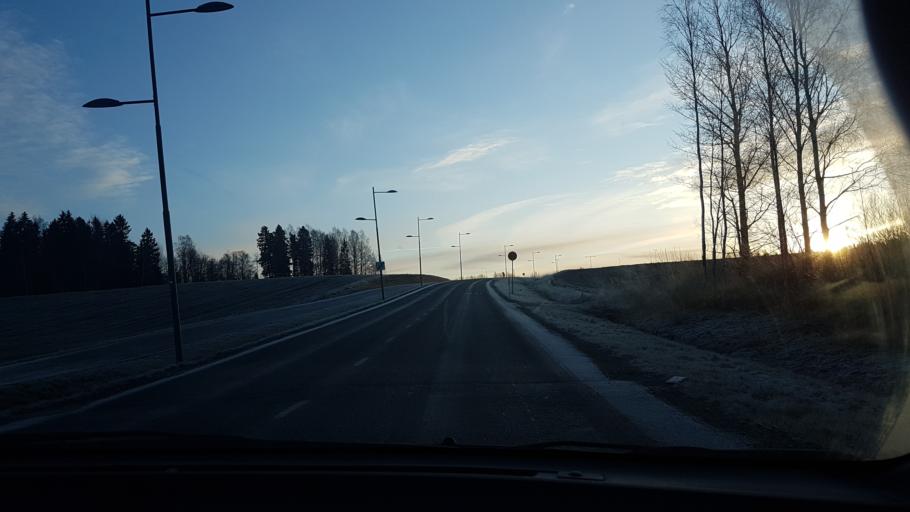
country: FI
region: Uusimaa
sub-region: Helsinki
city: Tuusula
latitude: 60.3791
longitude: 24.9912
